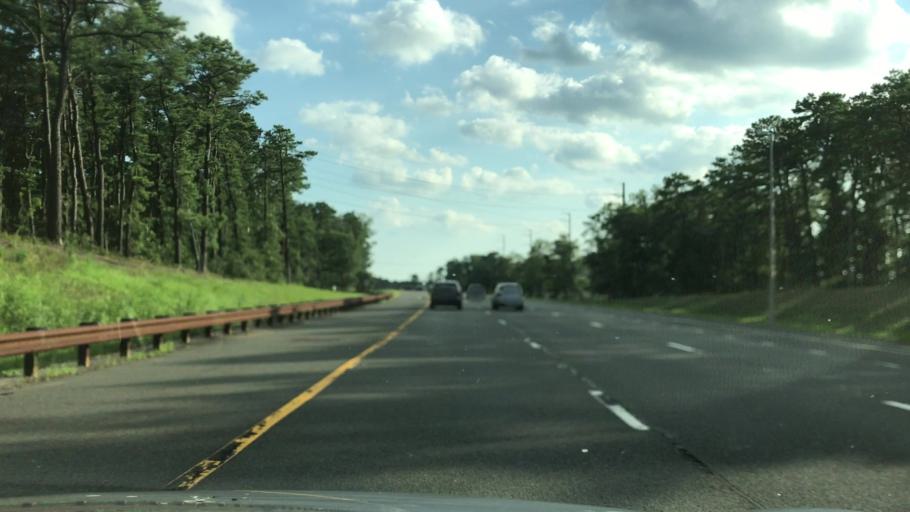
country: US
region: New Jersey
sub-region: Ocean County
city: Manahawkin
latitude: 39.7085
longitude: -74.2839
